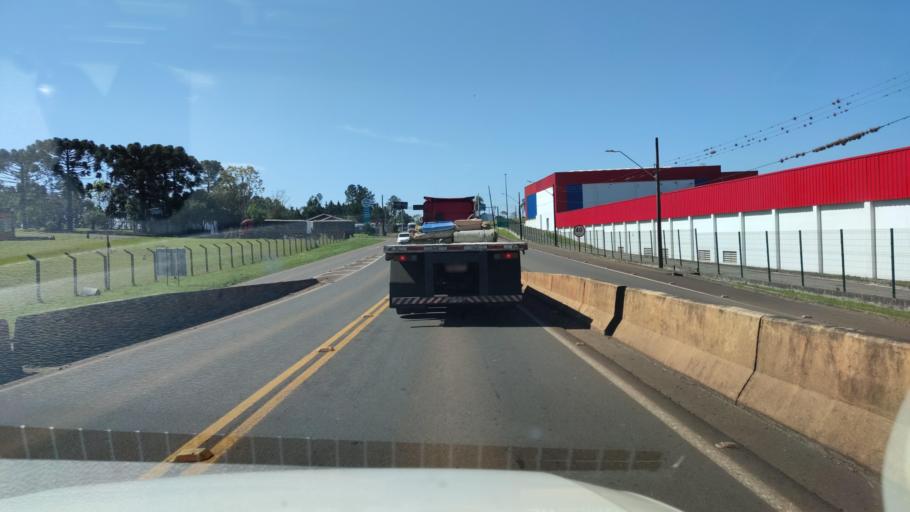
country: BR
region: Santa Catarina
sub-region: Sao Lourenco Do Oeste
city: Sao Lourenco dOeste
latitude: -26.3468
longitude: -52.8519
